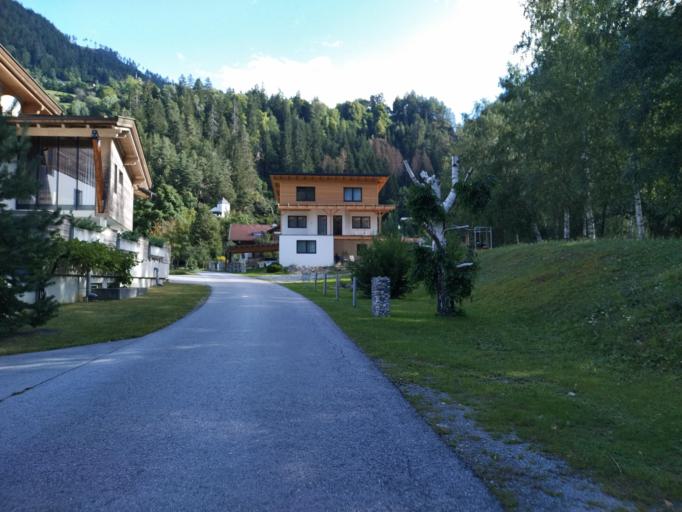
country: AT
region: Tyrol
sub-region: Politischer Bezirk Lienz
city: Hopfgarten in Defereggen
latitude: 46.9287
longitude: 12.5913
